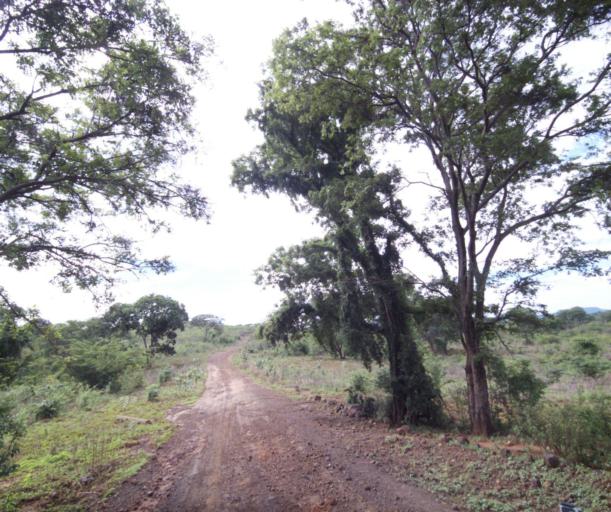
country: BR
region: Bahia
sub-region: Carinhanha
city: Carinhanha
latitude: -14.2294
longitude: -44.4302
